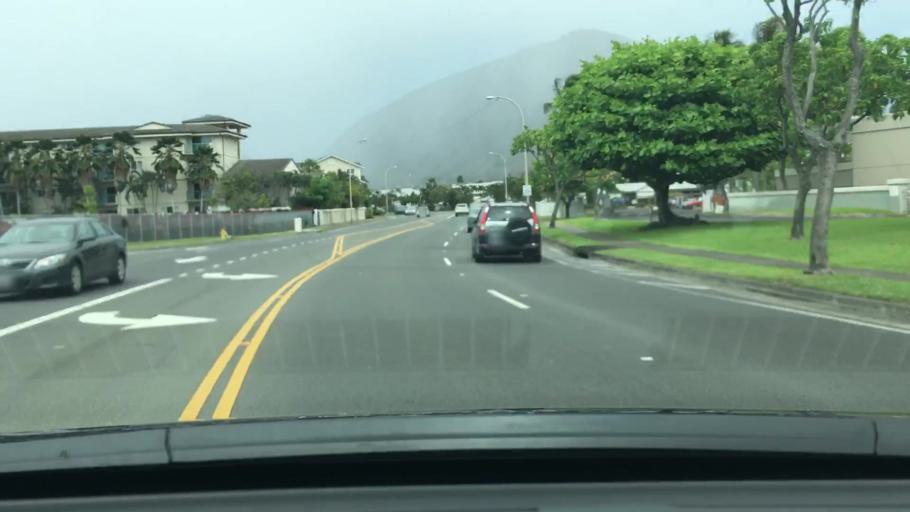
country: US
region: Hawaii
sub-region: Honolulu County
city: Waimanalo Beach
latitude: 21.2867
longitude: -157.7055
